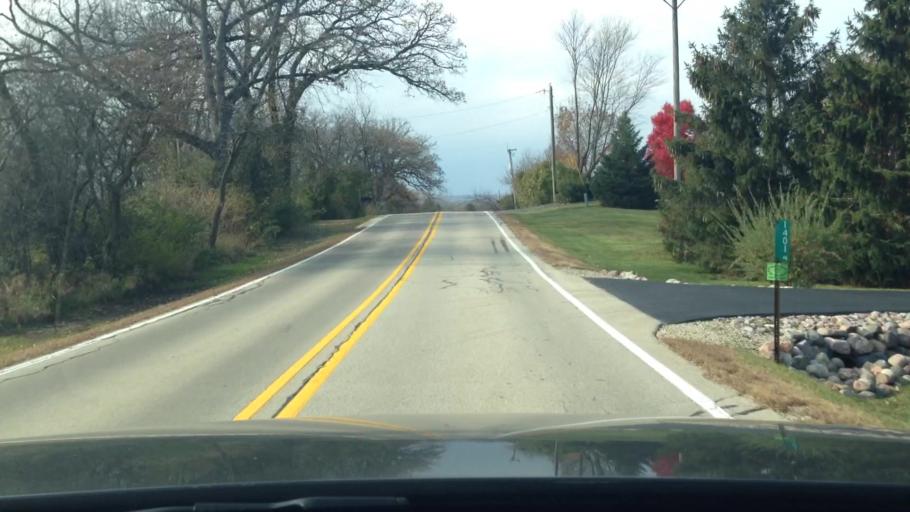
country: US
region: Illinois
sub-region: McHenry County
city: Woodstock
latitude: 42.2984
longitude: -88.4714
